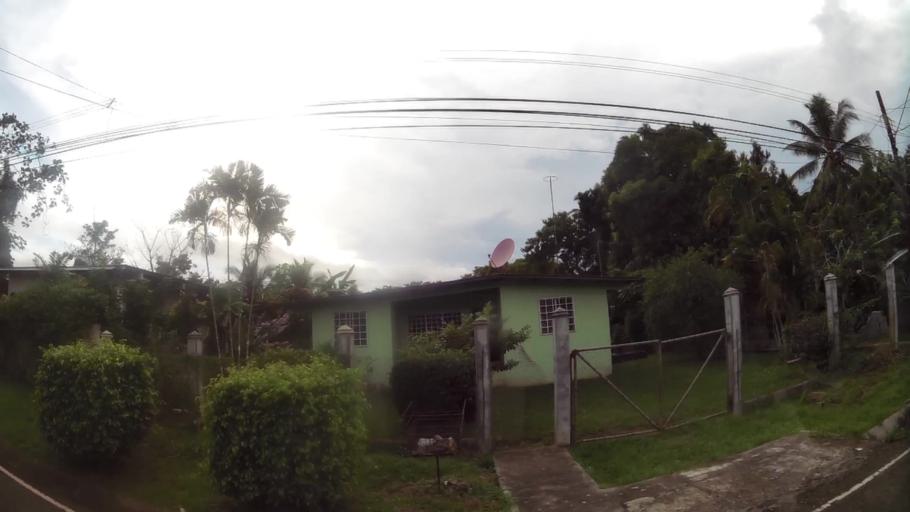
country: PA
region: Panama
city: El Coco
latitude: 8.8658
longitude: -79.8109
